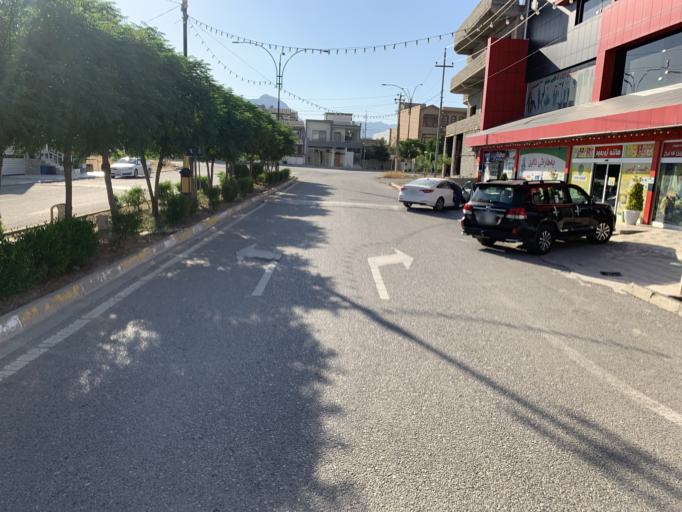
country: IQ
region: As Sulaymaniyah
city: Raniye
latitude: 36.2422
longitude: 44.8730
